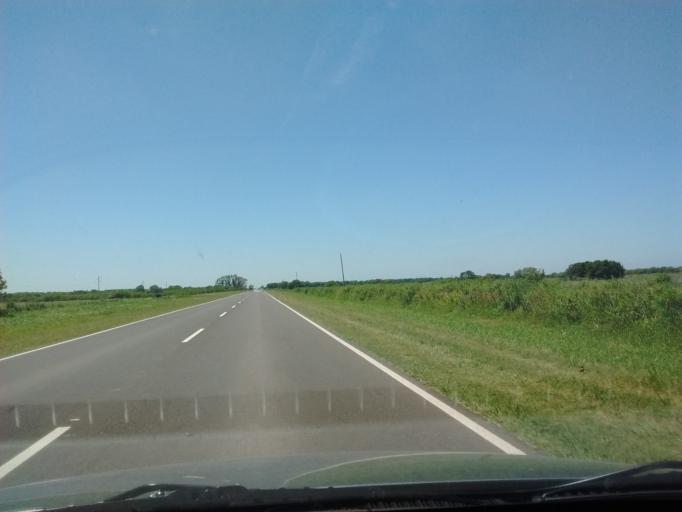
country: AR
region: Entre Rios
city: General Galarza
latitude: -32.8645
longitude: -59.7325
